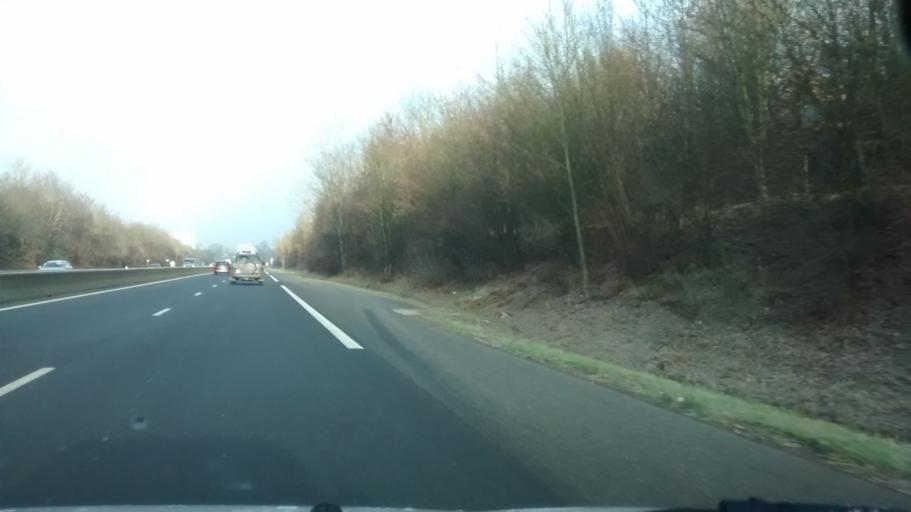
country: FR
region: Centre
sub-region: Departement d'Indre-et-Loire
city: Joue-les-Tours
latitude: 47.3341
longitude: 0.6721
